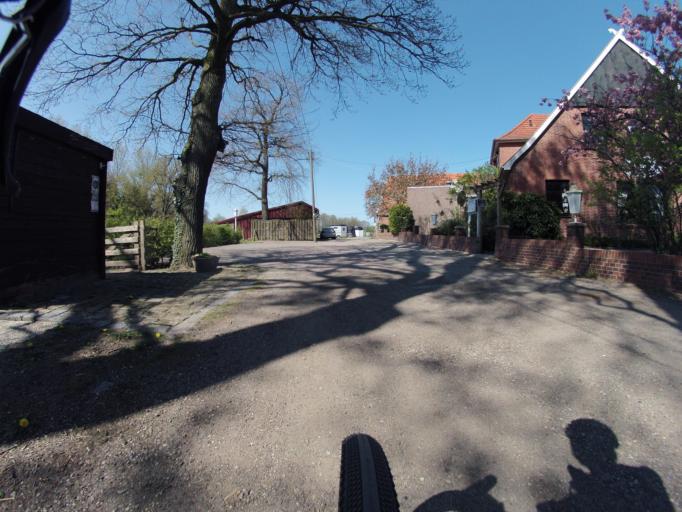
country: NL
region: Overijssel
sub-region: Gemeente Losser
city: Losser
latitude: 52.2739
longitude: 7.0285
